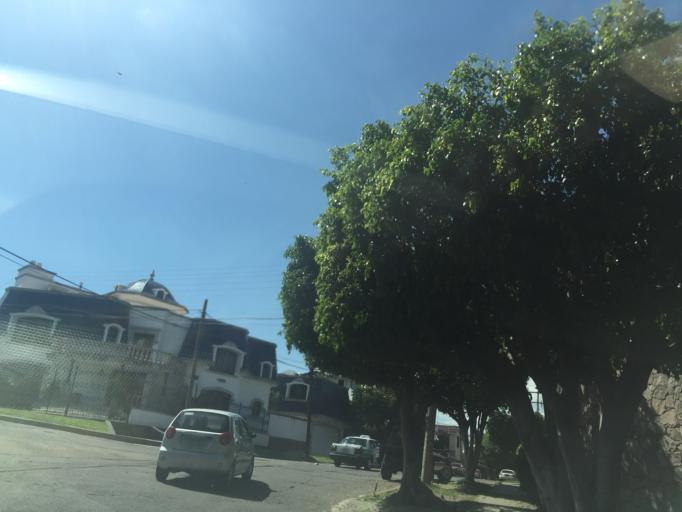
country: MX
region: Guanajuato
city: Leon
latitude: 21.1473
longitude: -101.6936
